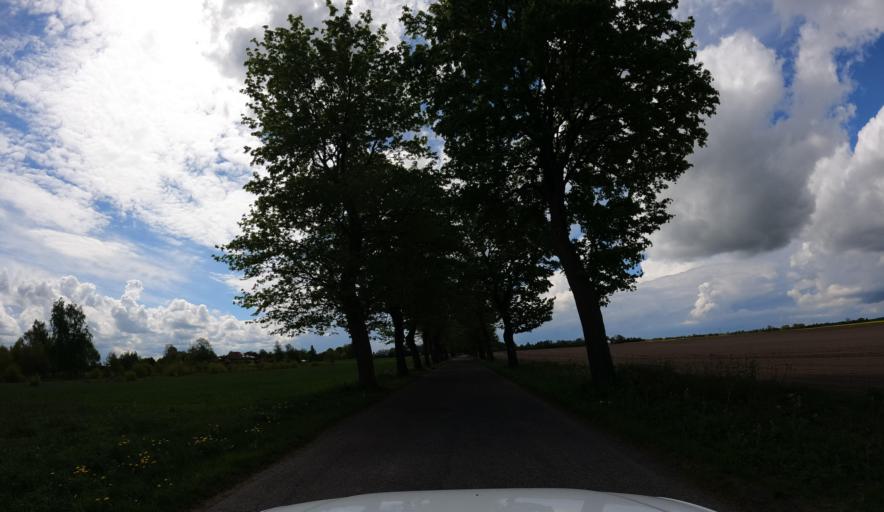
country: PL
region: West Pomeranian Voivodeship
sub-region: Powiat kamienski
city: Wolin
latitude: 53.8754
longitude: 14.6502
